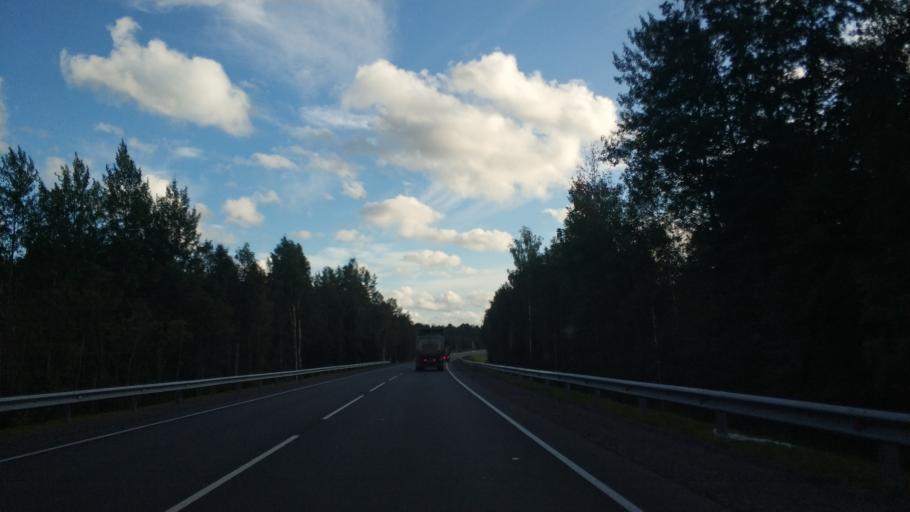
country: RU
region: Leningrad
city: Priozersk
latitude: 60.8643
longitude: 30.1590
